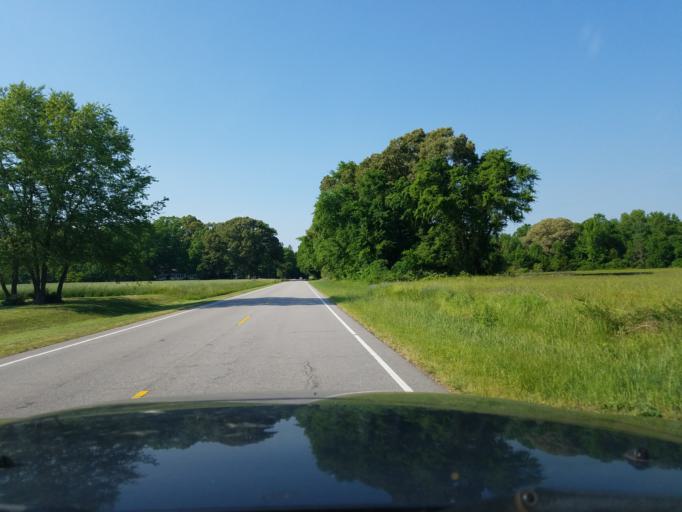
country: US
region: North Carolina
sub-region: Vance County
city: Henderson
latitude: 36.3818
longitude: -78.3691
